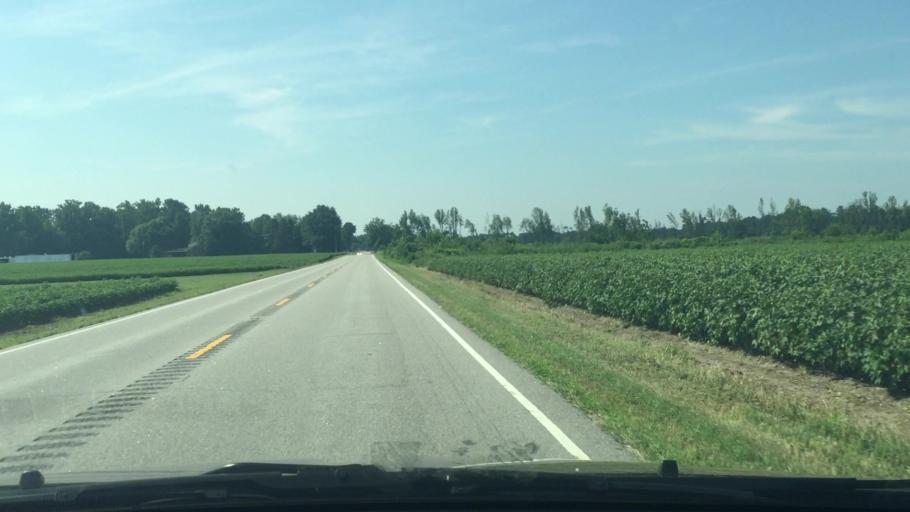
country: US
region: Virginia
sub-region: Southampton County
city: Courtland
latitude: 36.8022
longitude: -77.1285
